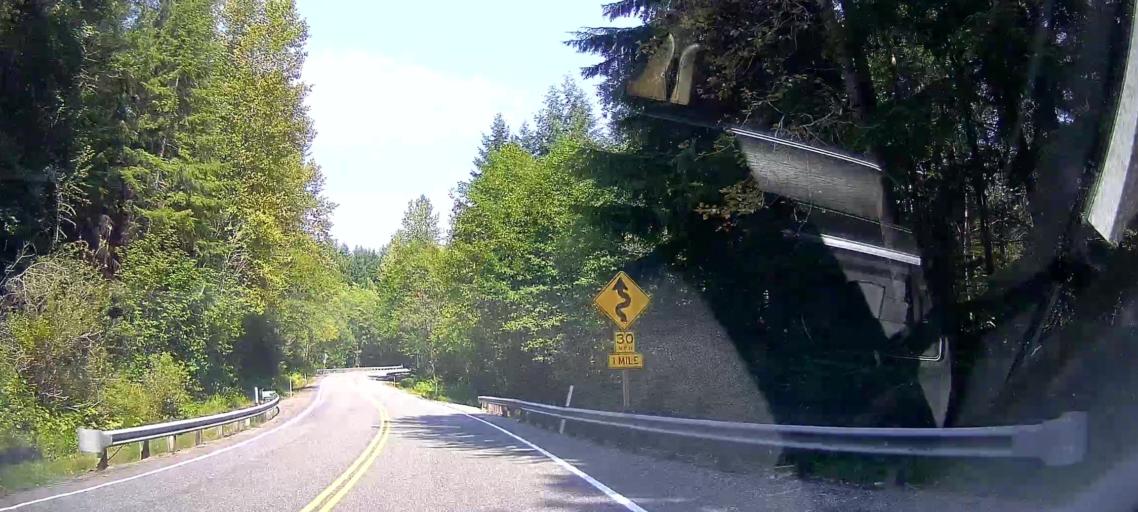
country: US
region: Washington
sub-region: Snohomish County
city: Bryant
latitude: 48.3330
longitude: -122.1322
